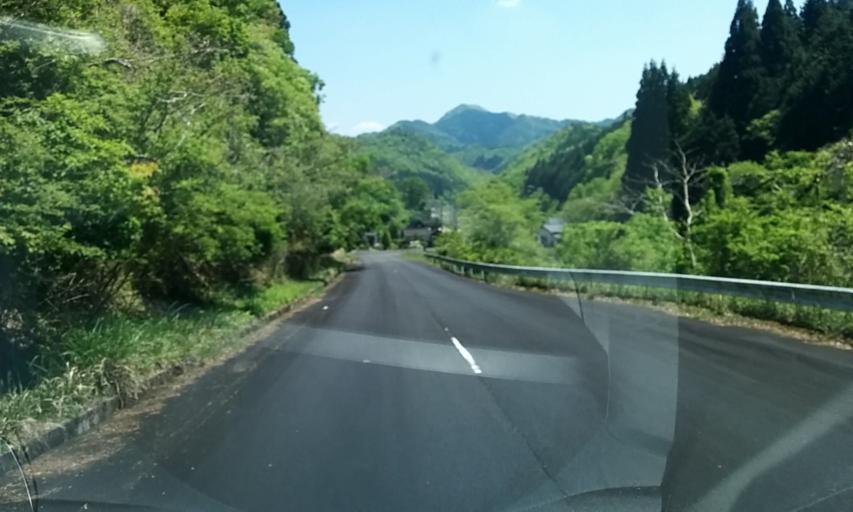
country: JP
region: Kyoto
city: Ayabe
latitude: 35.2250
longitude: 135.2849
